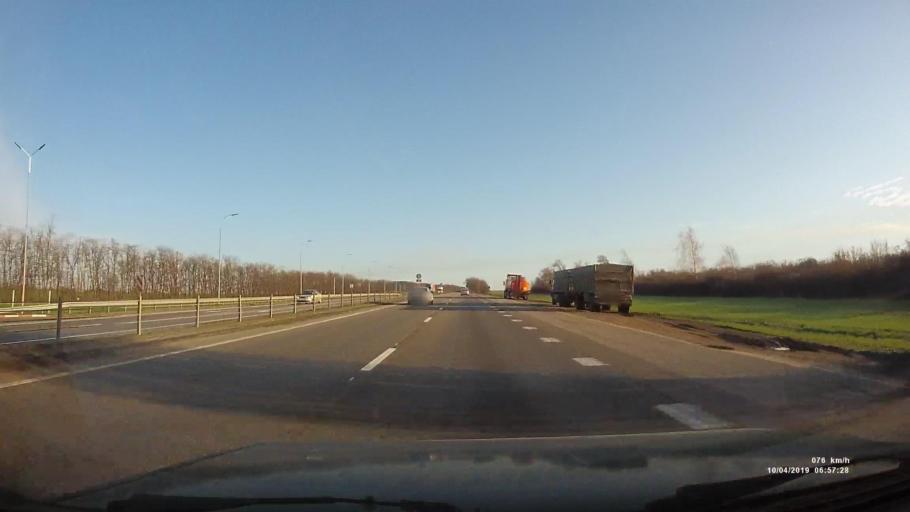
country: RU
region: Rostov
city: Grushevskaya
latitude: 47.5380
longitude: 39.9688
